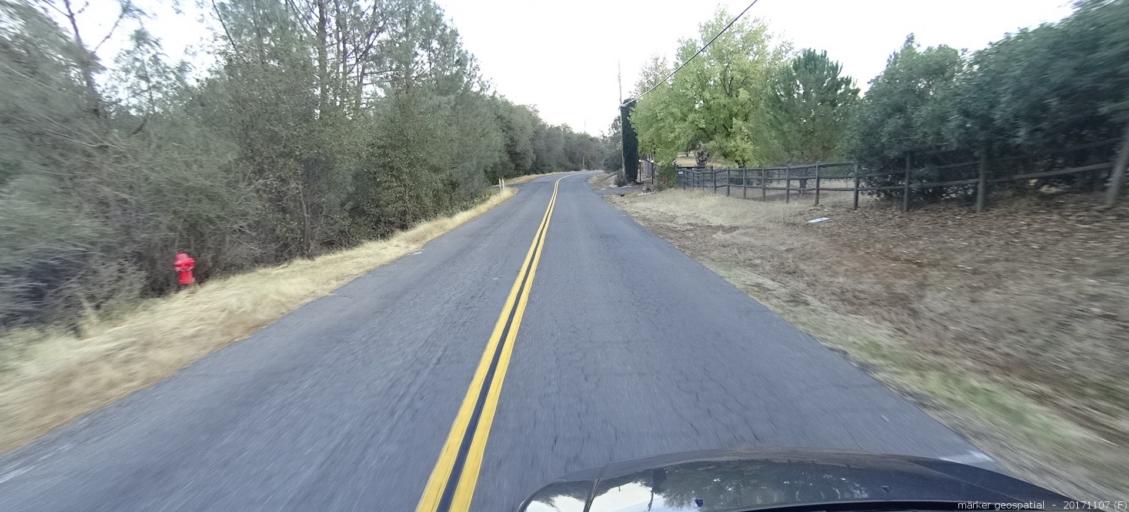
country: US
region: California
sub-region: Shasta County
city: Shasta
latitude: 40.5423
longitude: -122.4852
